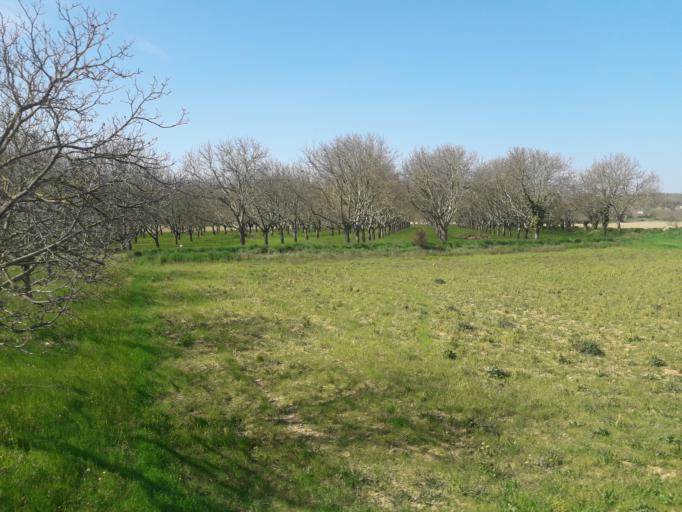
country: FR
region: Rhone-Alpes
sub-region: Departement de la Drome
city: Saint-Paul-les-Romans
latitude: 45.0729
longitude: 5.1409
